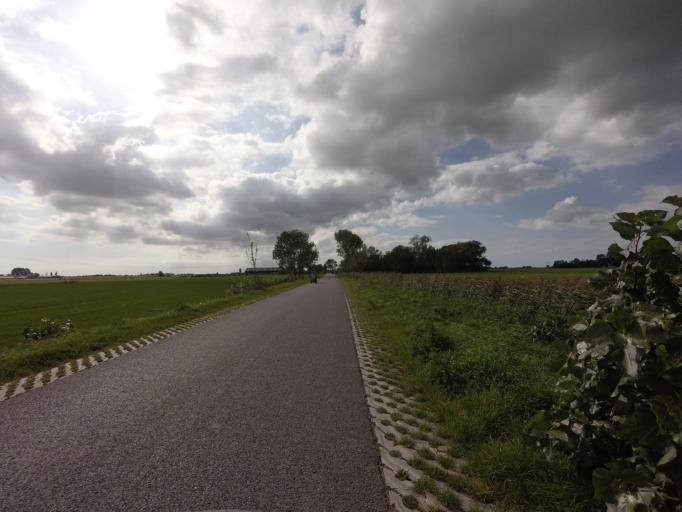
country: NL
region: Friesland
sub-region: Gemeente Littenseradiel
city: Wommels
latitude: 53.0704
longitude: 5.5921
